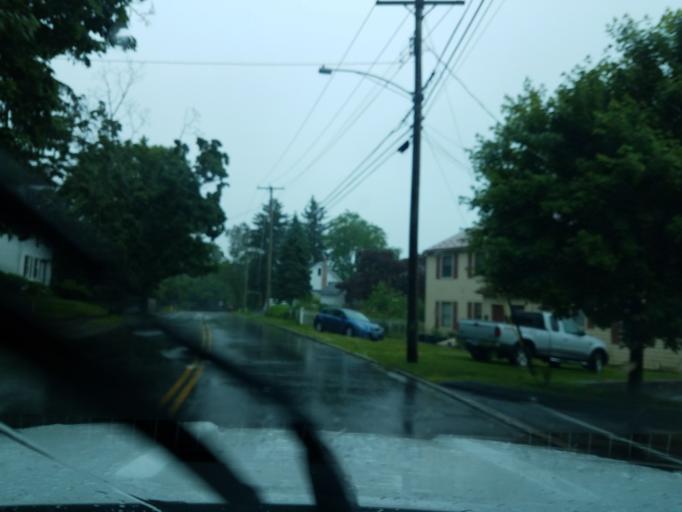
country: US
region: Connecticut
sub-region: New Haven County
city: City of Milford (balance)
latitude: 41.2220
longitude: -73.0721
